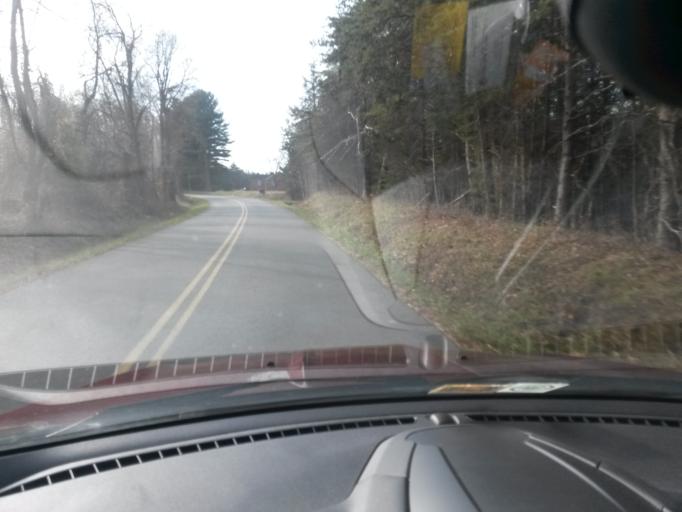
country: US
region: Virginia
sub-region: Botetourt County
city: Fincastle
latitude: 37.5737
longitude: -79.8817
